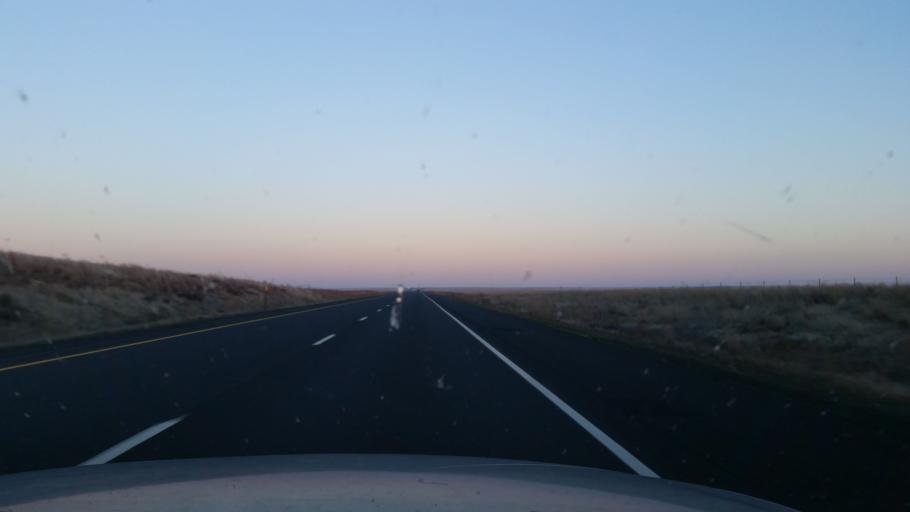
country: US
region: Washington
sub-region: Grant County
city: Warden
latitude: 47.0860
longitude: -118.7843
